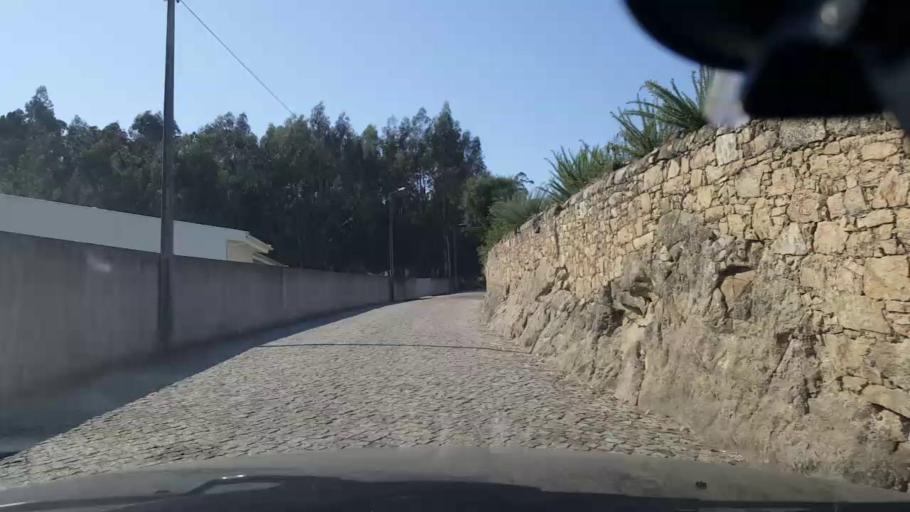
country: PT
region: Porto
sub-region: Povoa de Varzim
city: Pedroso
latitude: 41.4018
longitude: -8.6941
